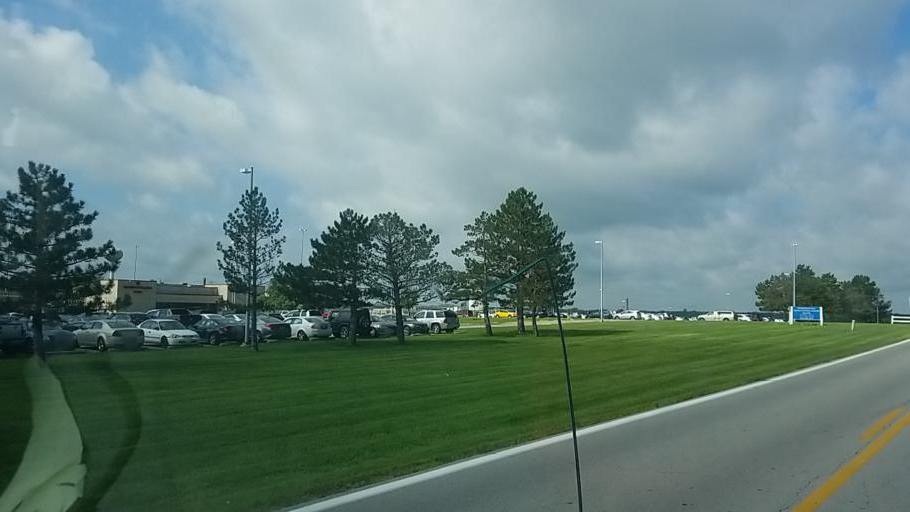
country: US
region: Ohio
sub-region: Franklin County
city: Grove City
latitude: 39.8027
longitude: -83.1475
